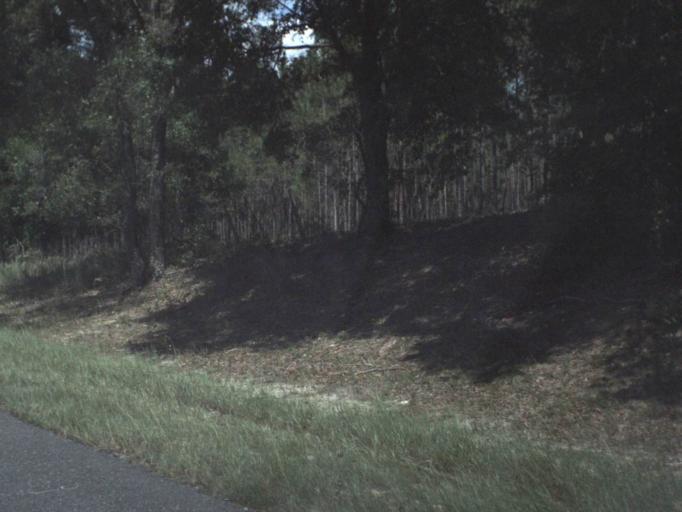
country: US
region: Florida
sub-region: Gilchrist County
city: Trenton
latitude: 29.7290
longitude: -82.7452
